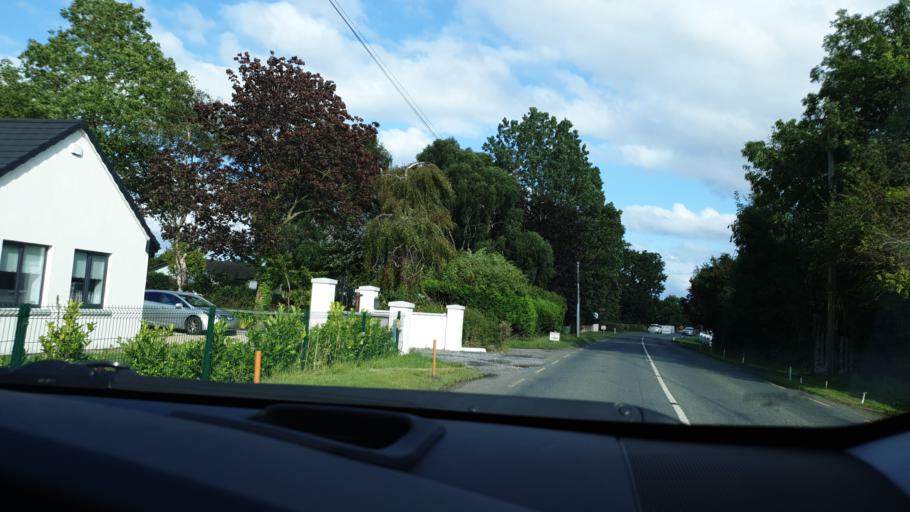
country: IE
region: Leinster
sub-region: An Mhi
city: Ashbourne
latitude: 53.4966
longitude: -6.4017
